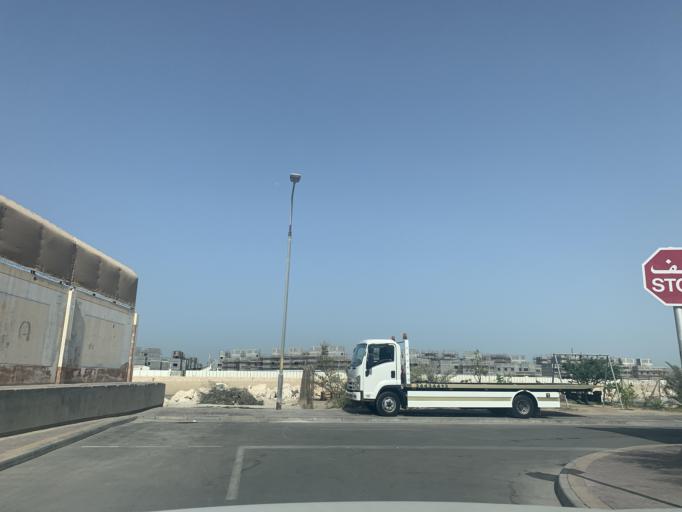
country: BH
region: Northern
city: Sitrah
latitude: 26.1624
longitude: 50.6292
